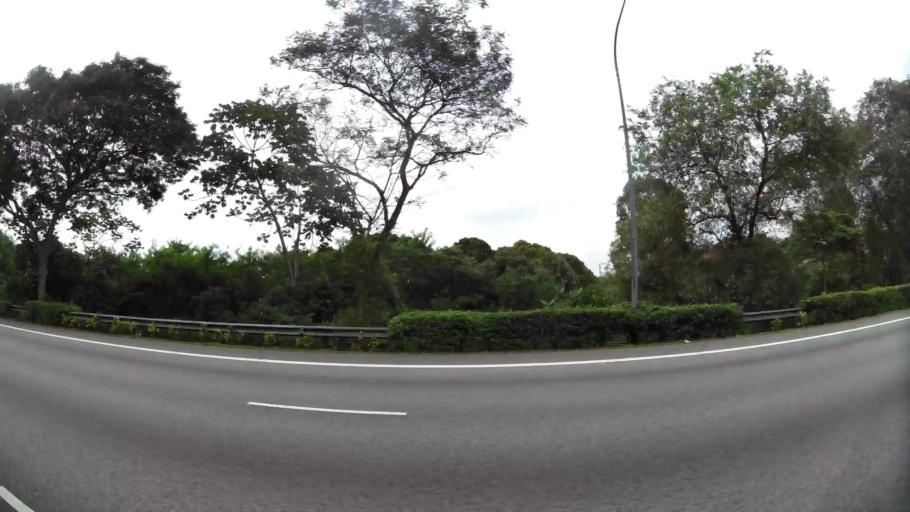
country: MY
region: Johor
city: Johor Bahru
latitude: 1.4256
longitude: 103.7775
